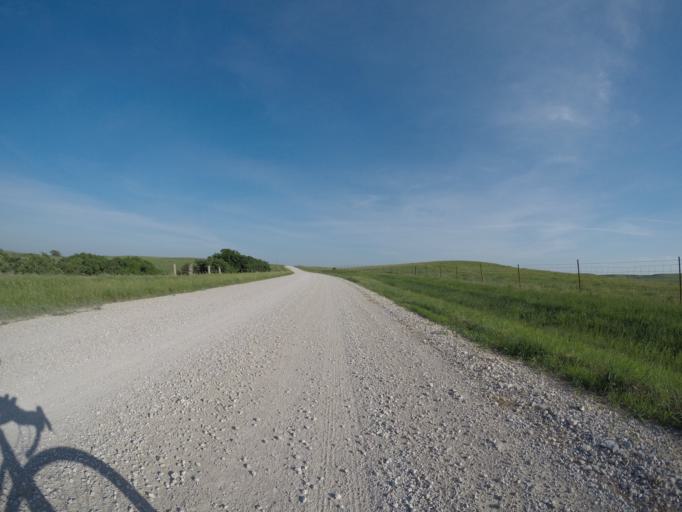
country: US
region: Kansas
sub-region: Riley County
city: Manhattan
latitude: 39.0506
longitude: -96.4957
